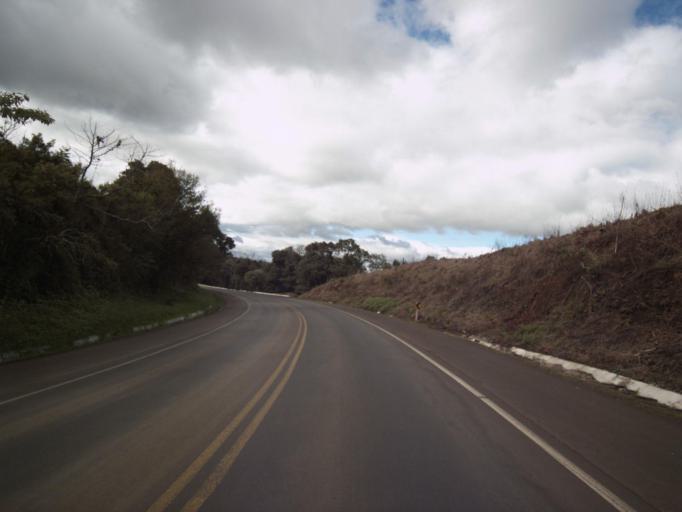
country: BR
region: Santa Catarina
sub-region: Concordia
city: Concordia
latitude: -27.3185
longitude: -51.9871
